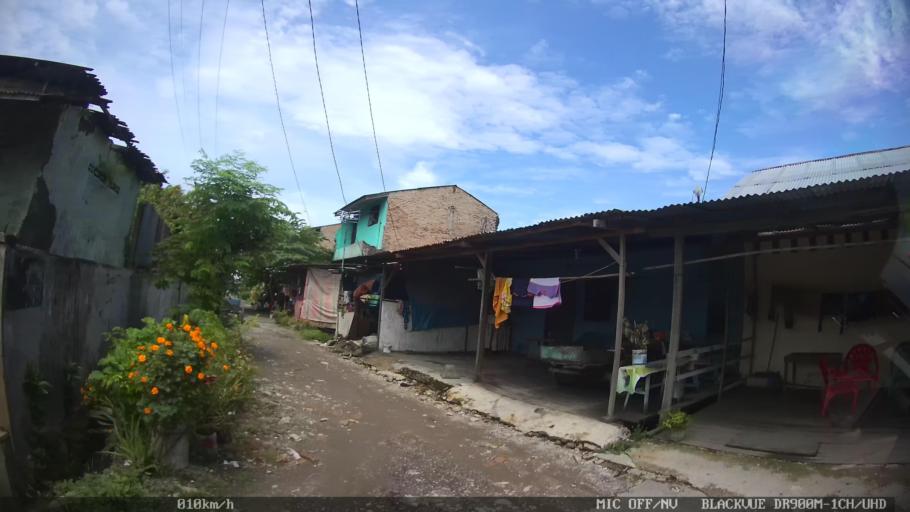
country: ID
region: North Sumatra
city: Medan
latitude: 3.5917
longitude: 98.7393
